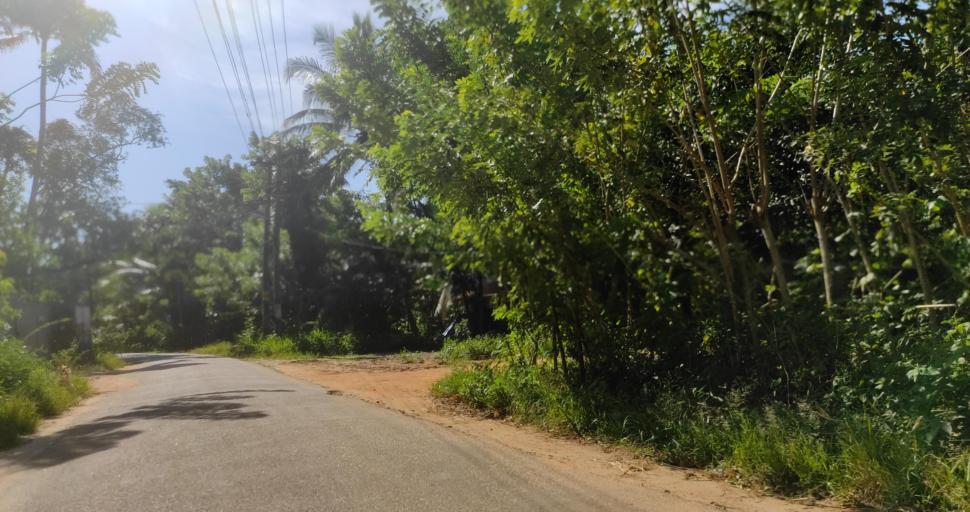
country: IN
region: Kerala
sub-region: Alappuzha
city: Shertallai
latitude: 9.6257
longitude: 76.3409
